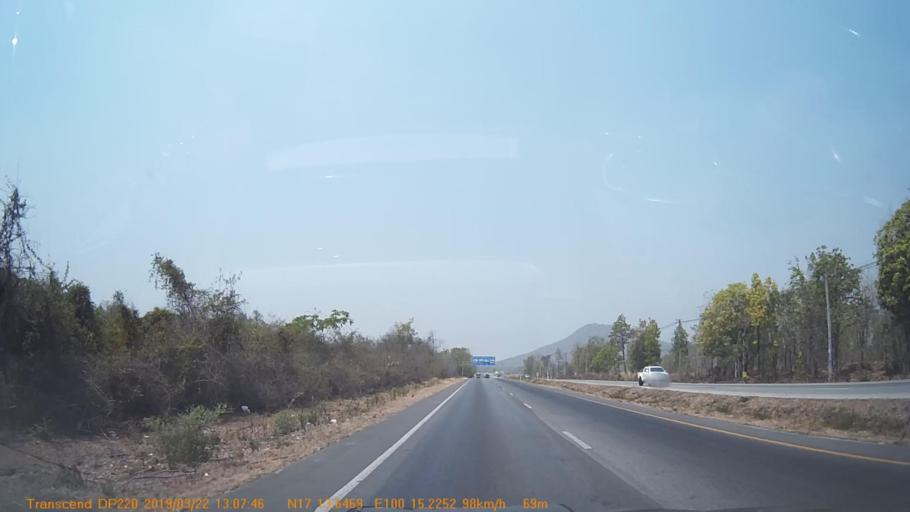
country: TH
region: Uttaradit
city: Phichai
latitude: 17.2278
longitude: 100.2536
